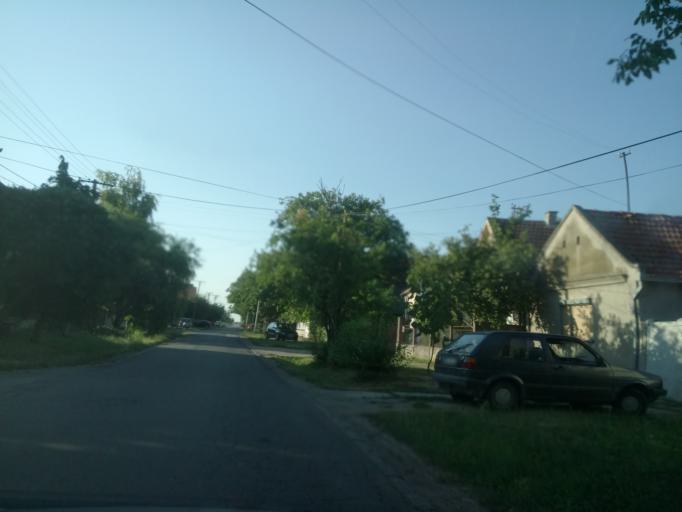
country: RS
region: Autonomna Pokrajina Vojvodina
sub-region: Sremski Okrug
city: Stara Pazova
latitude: 44.9903
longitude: 20.1694
